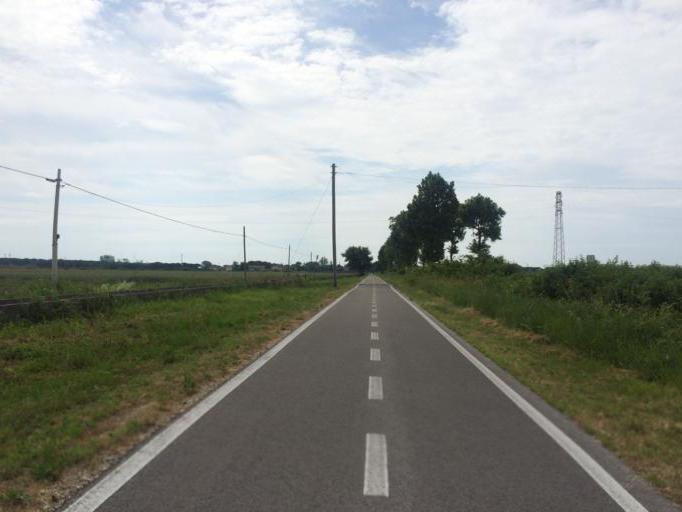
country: IT
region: Friuli Venezia Giulia
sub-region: Provincia di Udine
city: Aquileia
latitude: 45.7369
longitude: 13.3862
